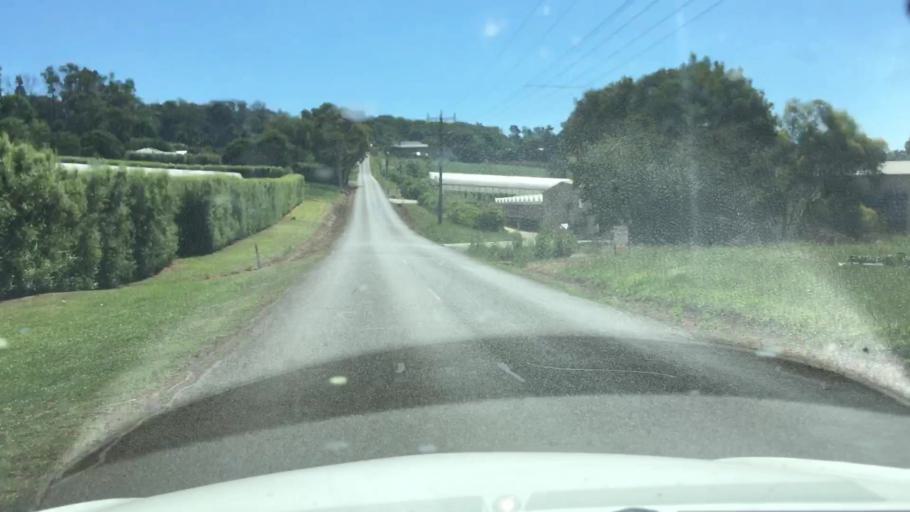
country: AU
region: Victoria
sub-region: Yarra Ranges
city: Mount Evelyn
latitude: -37.8193
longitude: 145.4199
